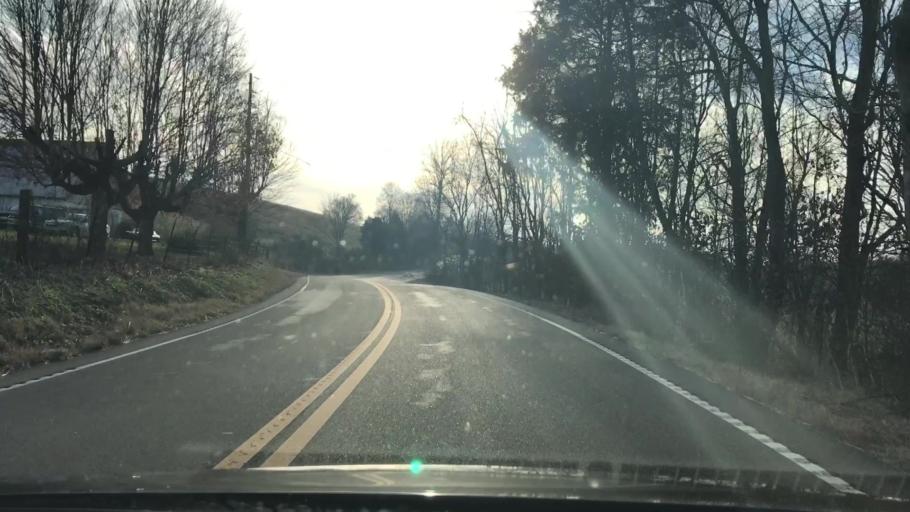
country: US
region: Tennessee
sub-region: Macon County
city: Red Boiling Springs
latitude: 36.6139
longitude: -85.8040
